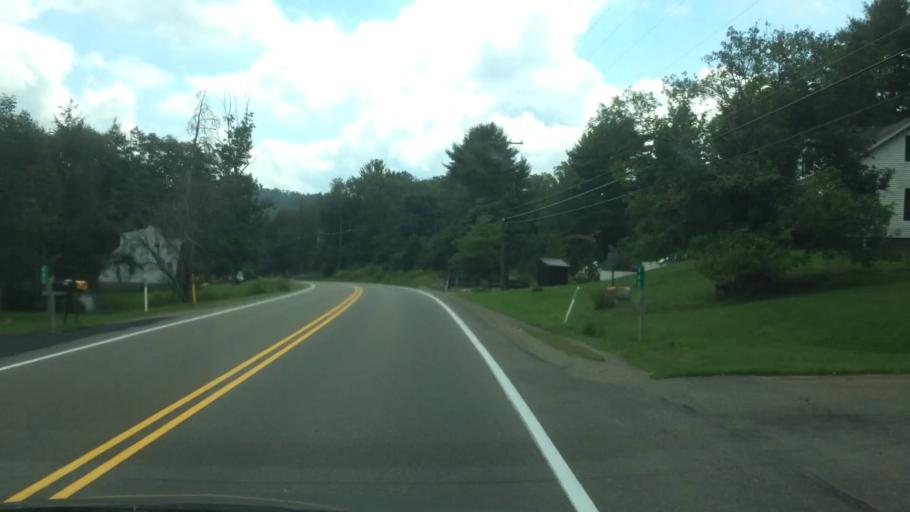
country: US
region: Pennsylvania
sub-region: McKean County
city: Bradford
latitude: 41.8941
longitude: -78.6071
